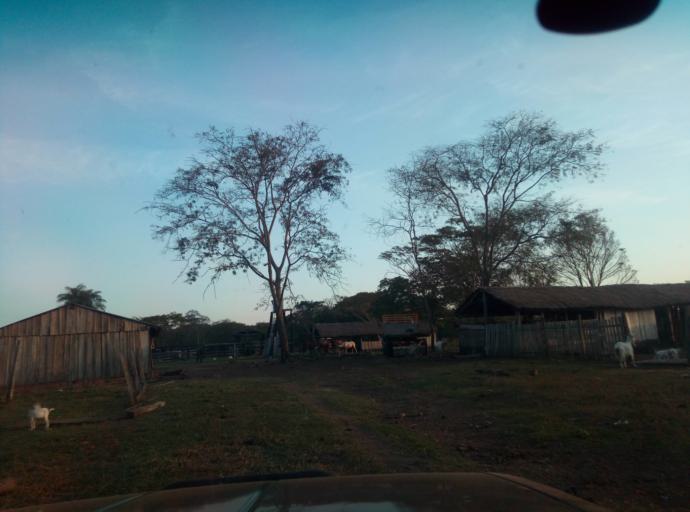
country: PY
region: Caaguazu
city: Yhu
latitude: -25.2059
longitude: -56.1054
